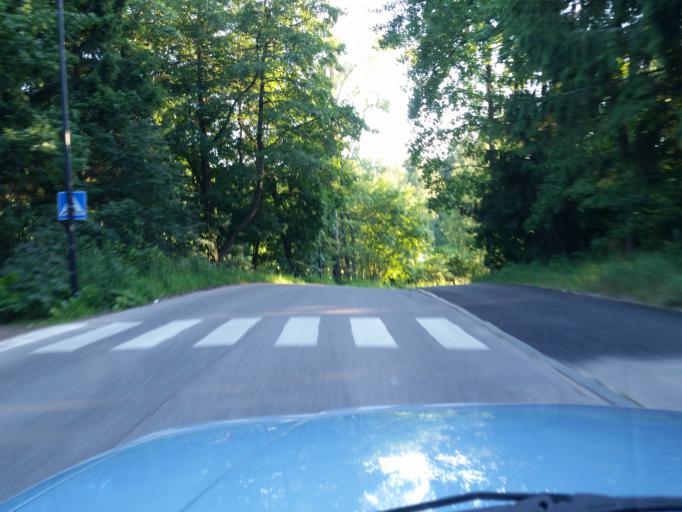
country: FI
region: Uusimaa
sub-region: Helsinki
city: Helsinki
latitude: 60.1919
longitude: 24.8926
